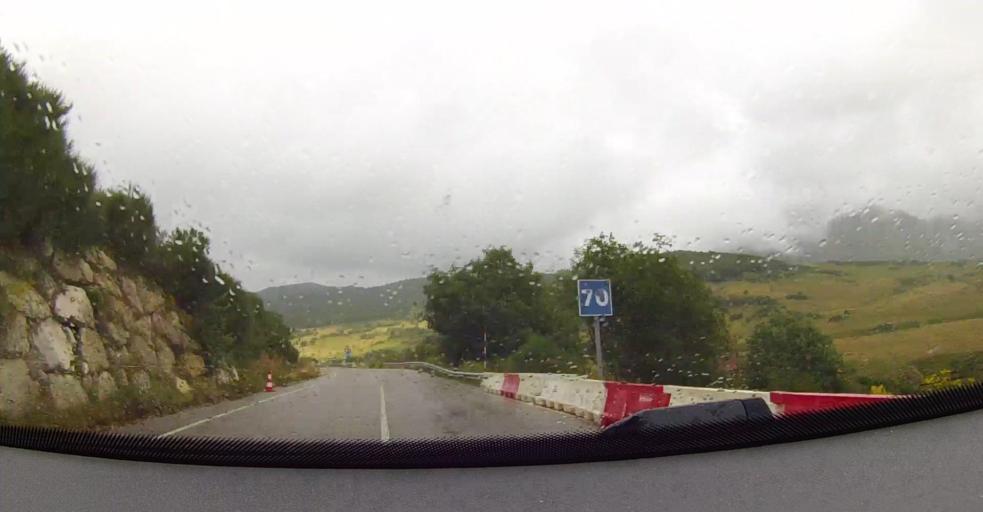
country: ES
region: Castille and Leon
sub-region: Provincia de Leon
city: Marana
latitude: 43.0714
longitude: -5.2021
